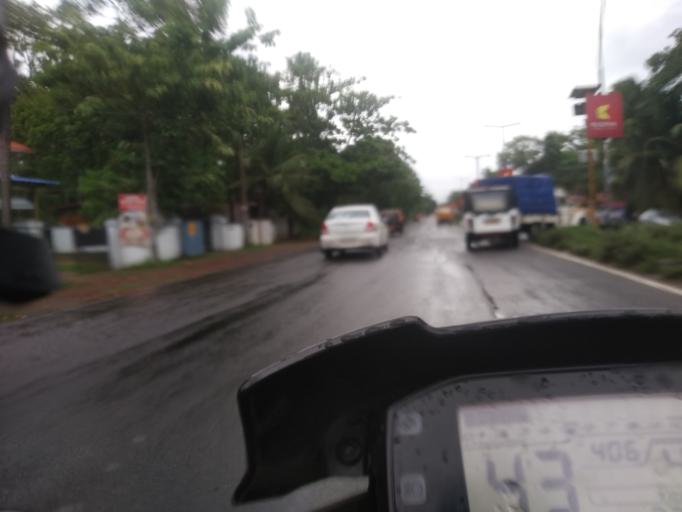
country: IN
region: Kerala
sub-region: Alappuzha
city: Vayalar
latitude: 9.7362
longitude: 76.3184
